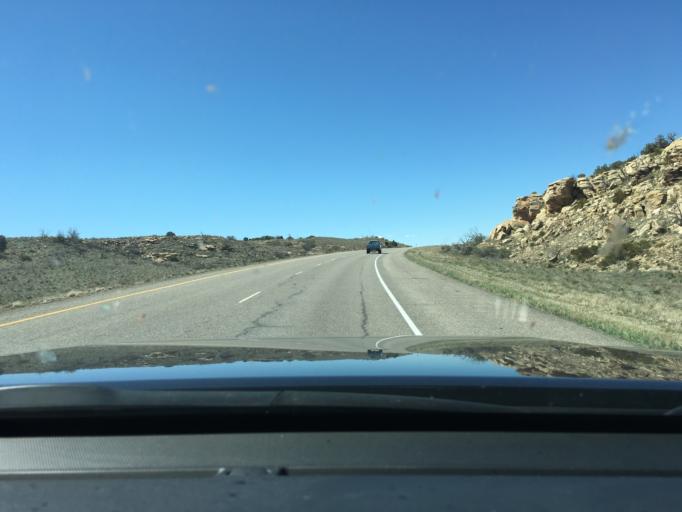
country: US
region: Colorado
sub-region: Mesa County
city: Loma
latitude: 39.1885
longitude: -109.0356
